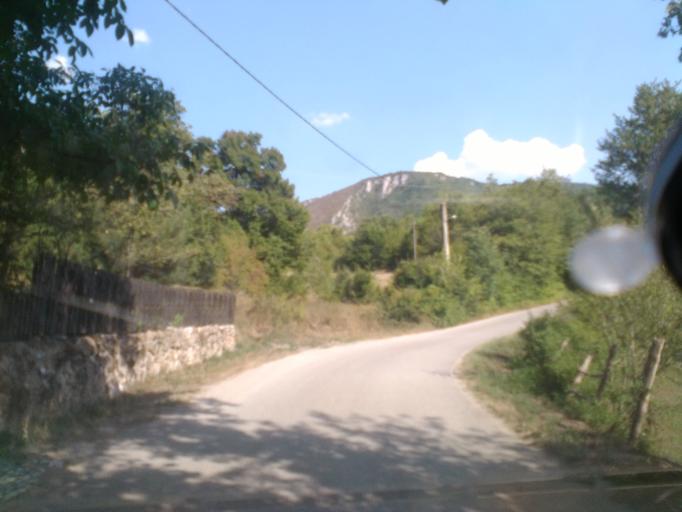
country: BA
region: Federation of Bosnia and Herzegovina
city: Orasac
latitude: 44.4953
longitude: 16.1361
